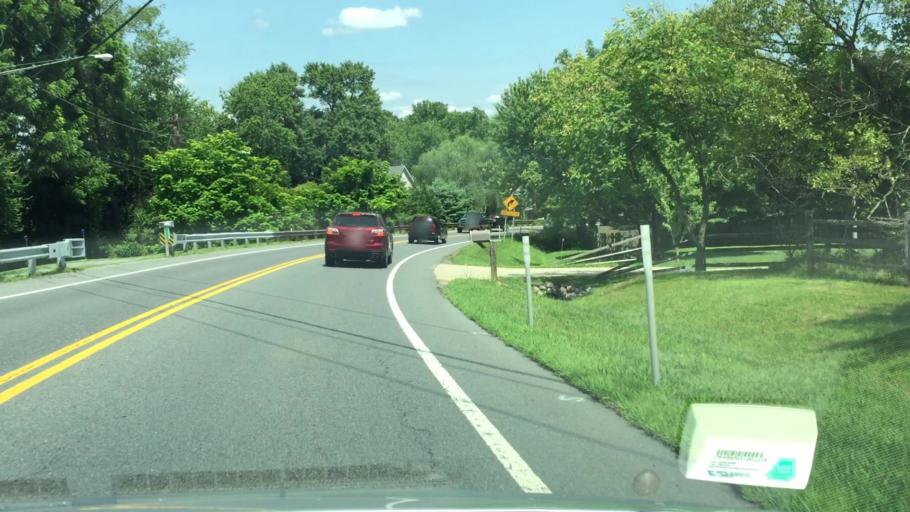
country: US
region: Maryland
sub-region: Montgomery County
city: Layhill
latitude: 39.0932
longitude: -77.0399
